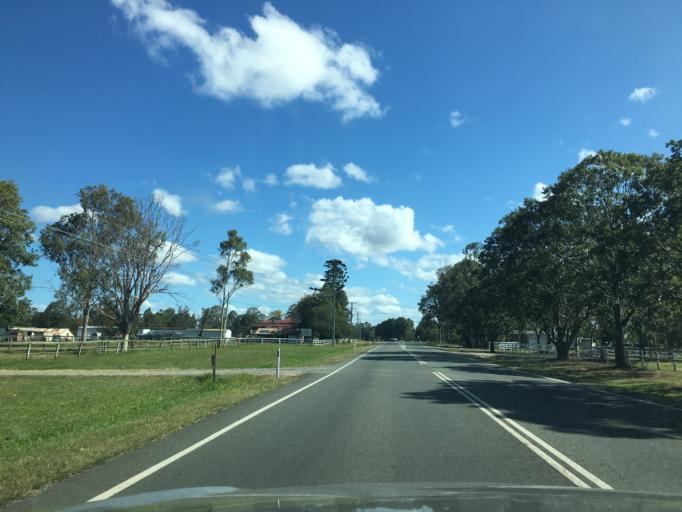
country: AU
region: Queensland
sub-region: Logan
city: Waterford West
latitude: -27.7121
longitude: 153.1306
